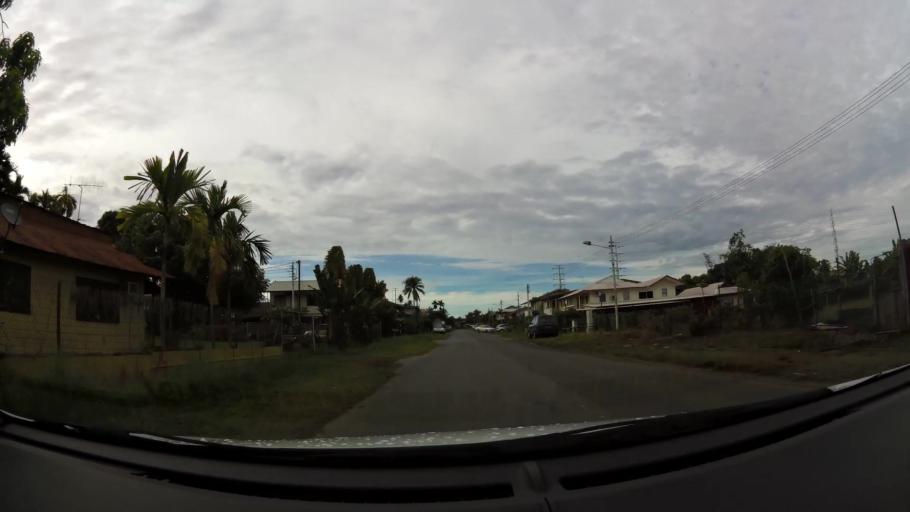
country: BN
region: Belait
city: Seria
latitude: 4.6167
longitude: 114.3471
